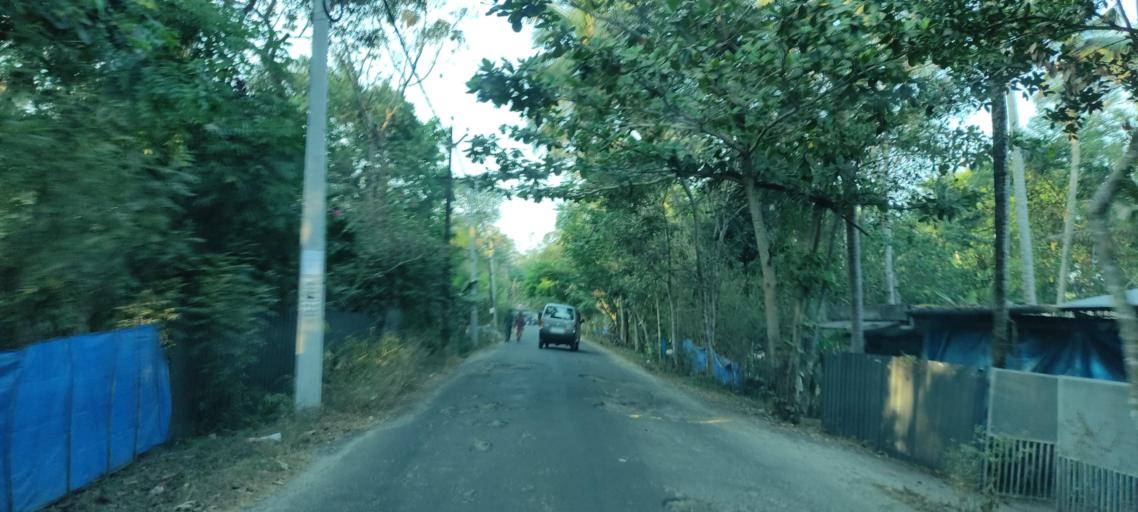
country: IN
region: Kerala
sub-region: Alappuzha
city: Kutiatodu
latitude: 9.7679
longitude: 76.3532
